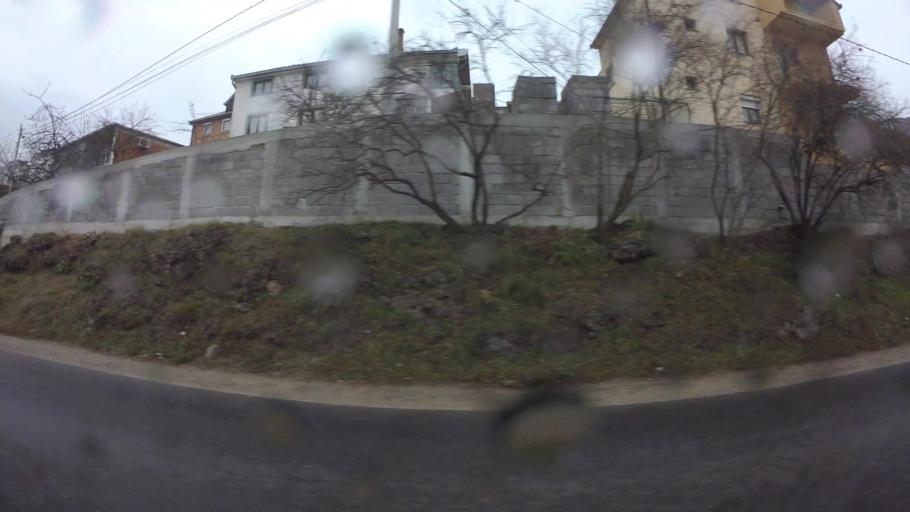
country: BA
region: Federation of Bosnia and Herzegovina
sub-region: Hercegovacko-Bosanski Kanton
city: Mostar
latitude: 43.3503
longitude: 17.8164
